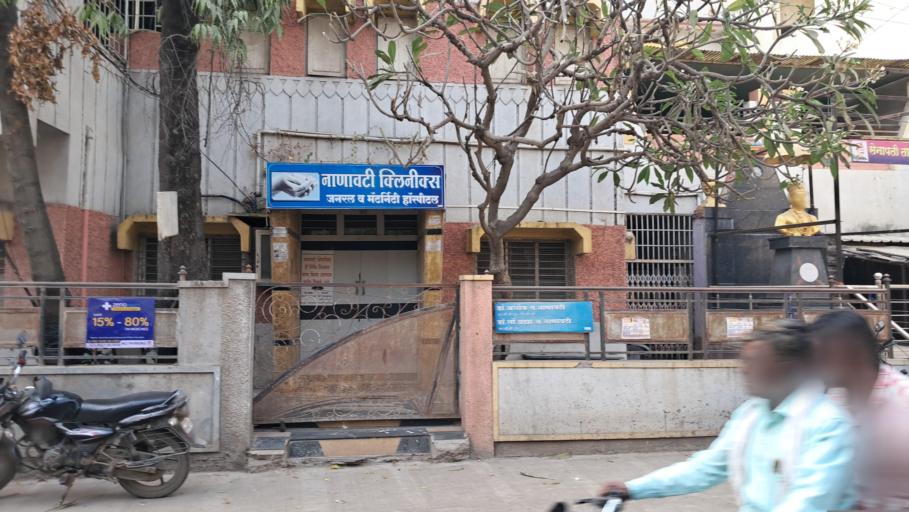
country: IN
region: Maharashtra
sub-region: Nashik Division
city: Yeola
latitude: 20.0399
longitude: 74.4899
